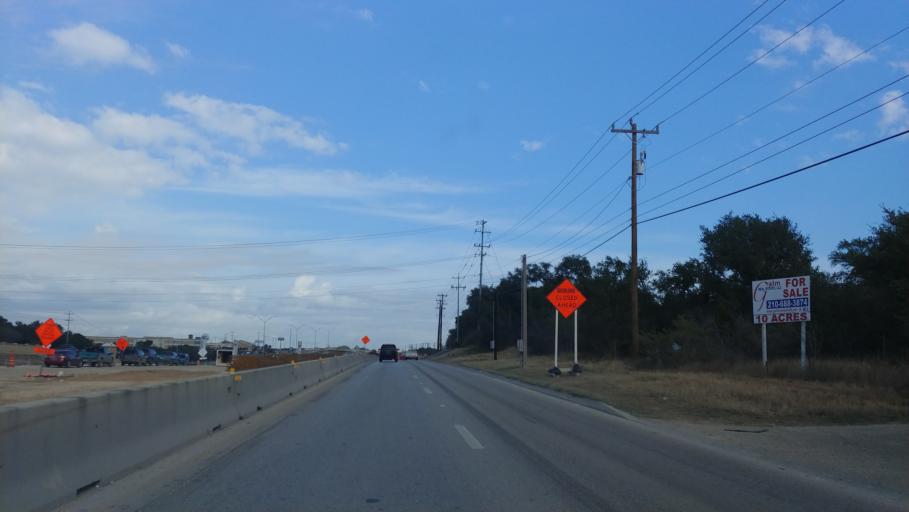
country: US
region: Texas
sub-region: Bexar County
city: Leon Valley
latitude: 29.4422
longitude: -98.7110
